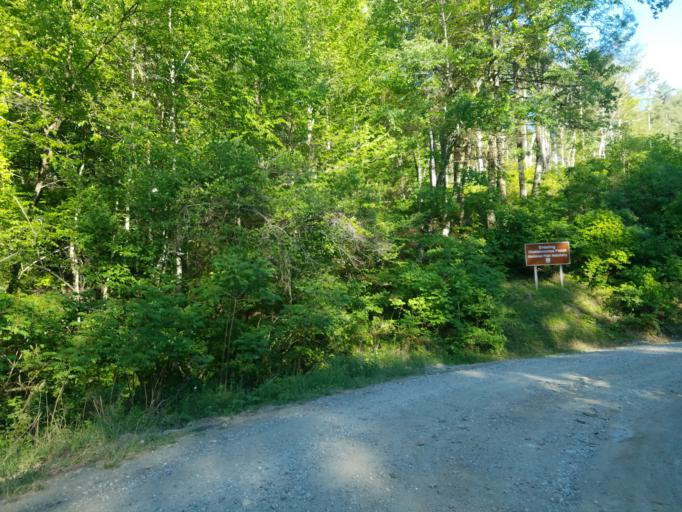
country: US
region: Georgia
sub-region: Fannin County
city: Blue Ridge
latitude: 34.7085
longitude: -84.1495
